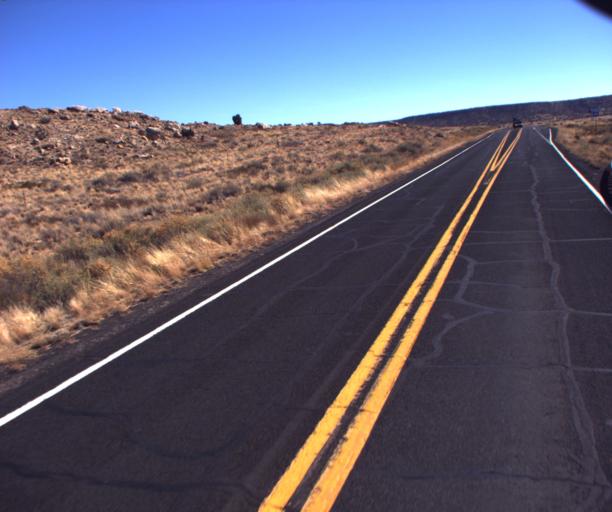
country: US
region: Arizona
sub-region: Navajo County
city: First Mesa
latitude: 35.8343
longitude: -110.2975
